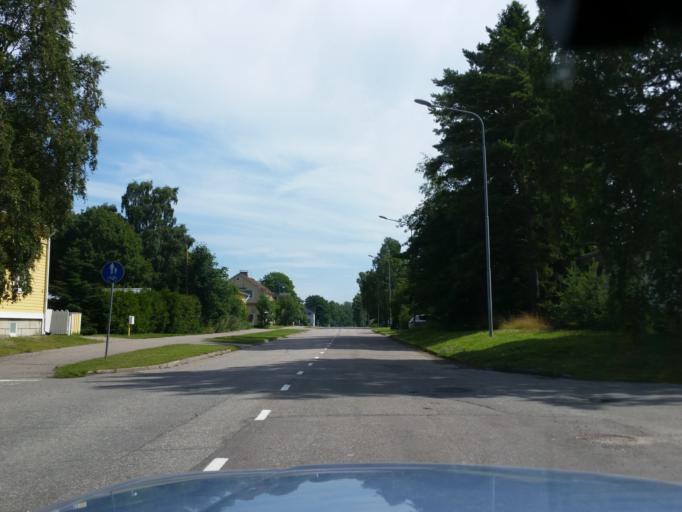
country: FI
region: Uusimaa
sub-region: Raaseporin
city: Hanko
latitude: 59.8339
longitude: 22.9489
